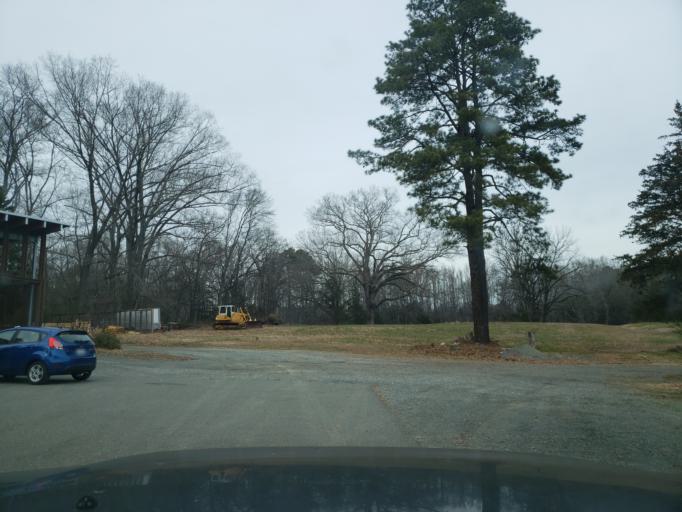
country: US
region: North Carolina
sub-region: Orange County
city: Chapel Hill
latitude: 35.9715
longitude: -79.0047
